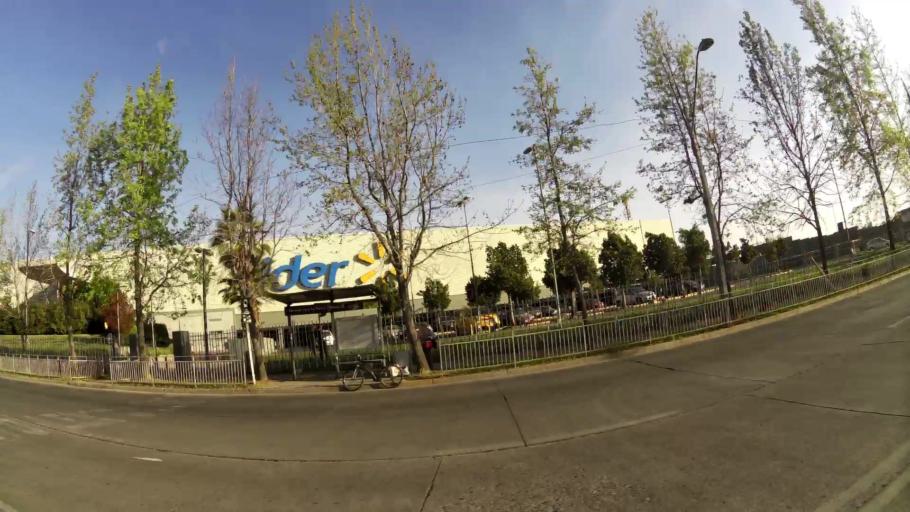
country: CL
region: Santiago Metropolitan
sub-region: Provincia de Cordillera
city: Puente Alto
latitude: -33.5437
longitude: -70.5715
